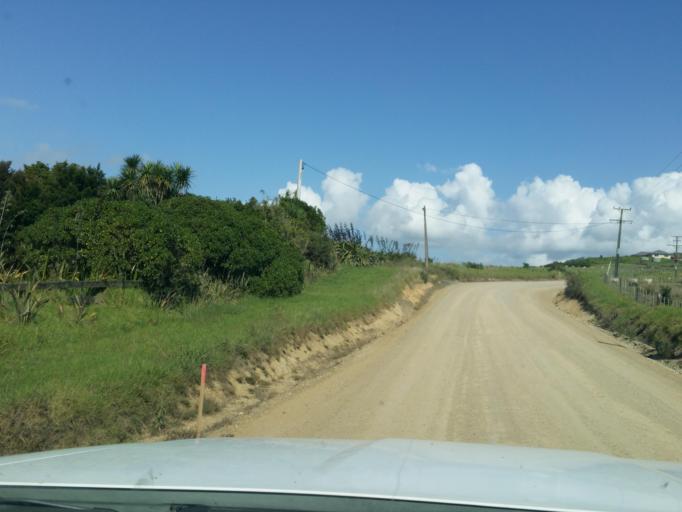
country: NZ
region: Auckland
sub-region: Auckland
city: Wellsford
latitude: -36.1409
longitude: 174.5394
